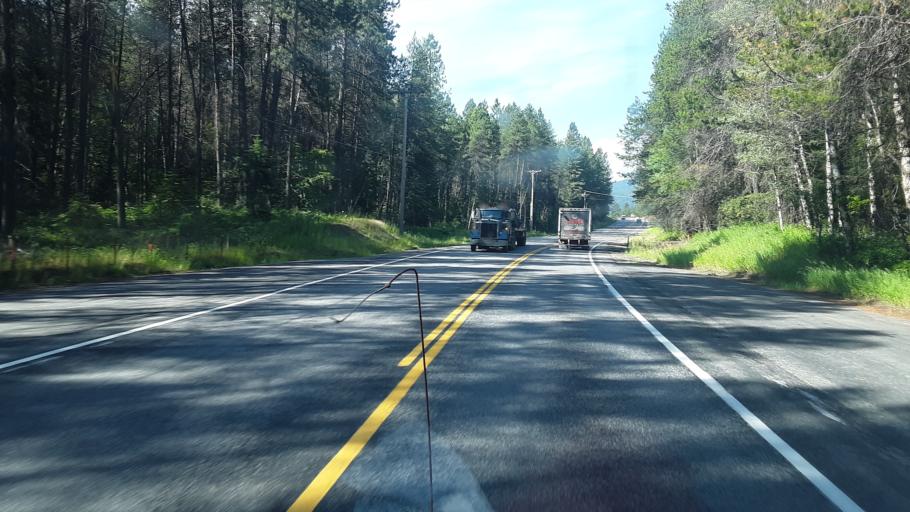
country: US
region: Idaho
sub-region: Boundary County
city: Bonners Ferry
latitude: 48.5278
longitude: -116.4314
